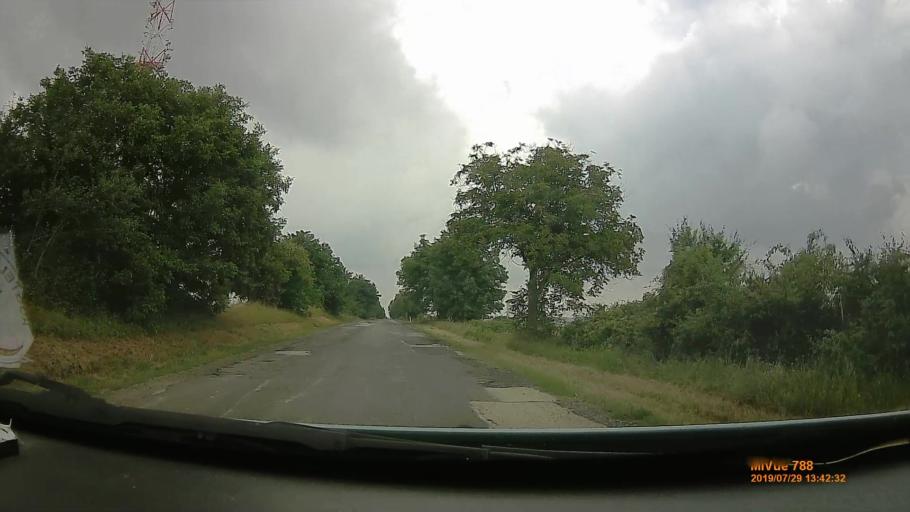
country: HU
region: Somogy
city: Balatonfoldvar
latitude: 46.8084
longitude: 17.9286
